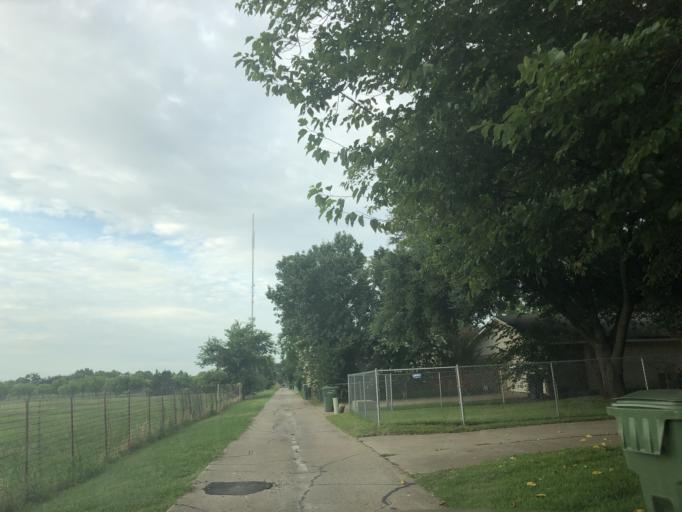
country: US
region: Texas
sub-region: Dallas County
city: Sunnyvale
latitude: 32.8471
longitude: -96.5639
